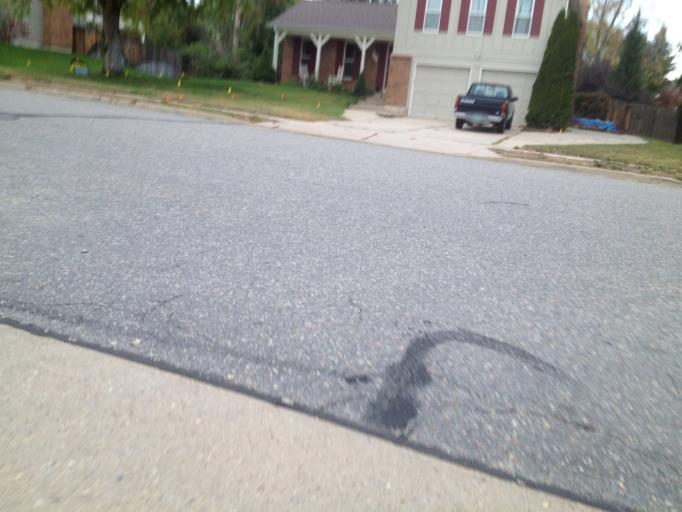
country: US
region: Colorado
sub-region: Boulder County
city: Louisville
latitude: 39.9918
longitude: -105.1400
